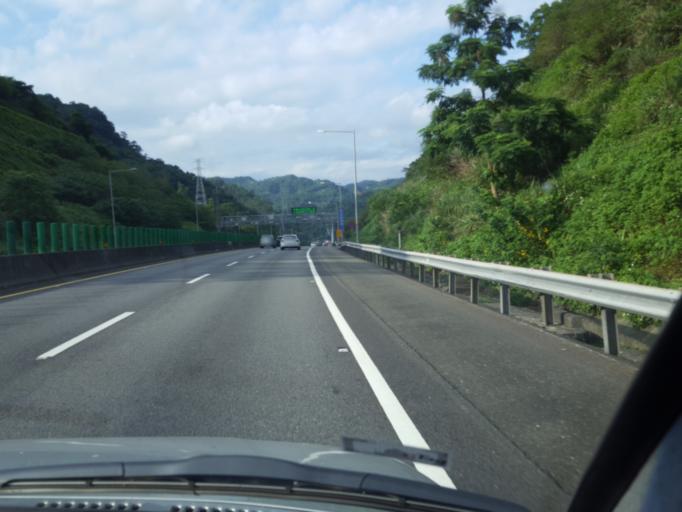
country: TW
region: Taipei
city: Taipei
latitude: 24.9949
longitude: 121.6524
